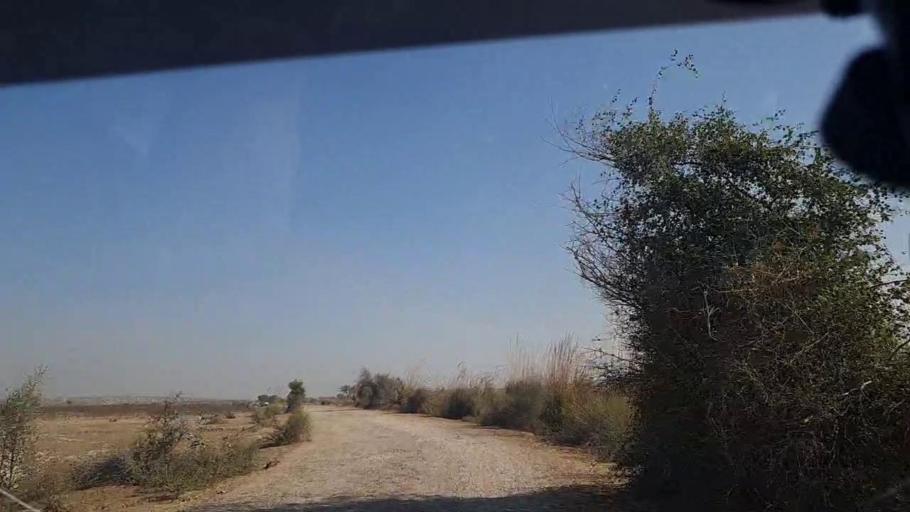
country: PK
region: Sindh
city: Khanpur
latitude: 27.5586
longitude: 69.3276
